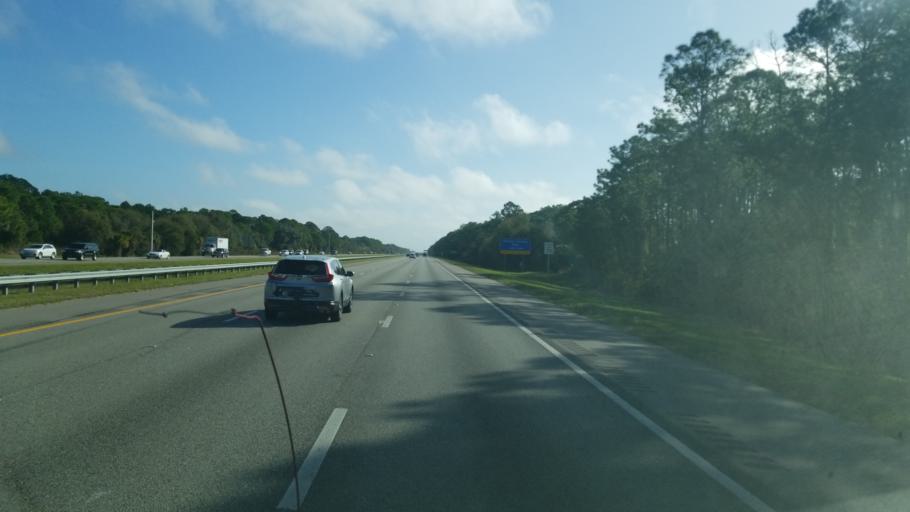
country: US
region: Florida
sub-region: Sarasota County
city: North Port
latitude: 27.0990
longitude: -82.1927
